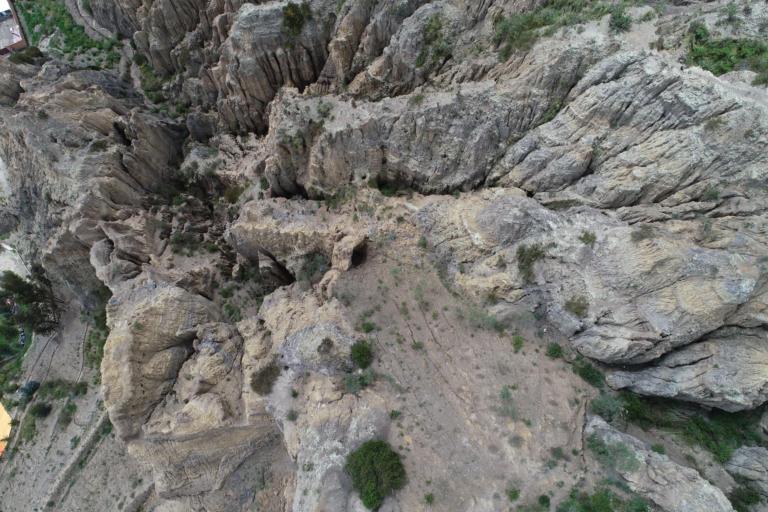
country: BO
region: La Paz
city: La Paz
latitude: -16.5005
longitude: -68.0803
